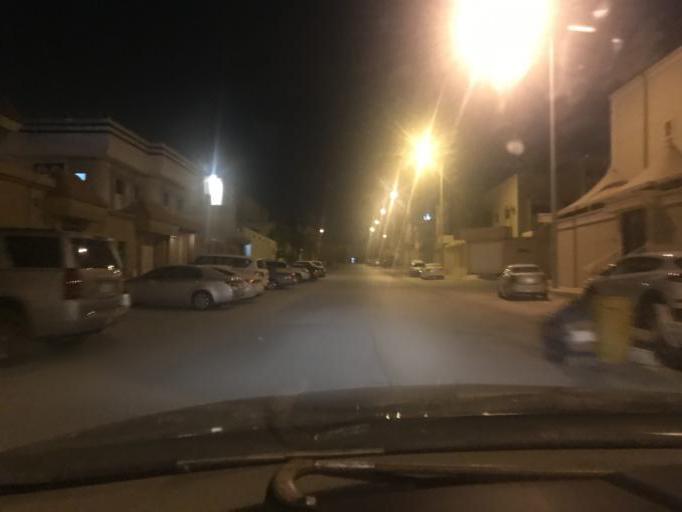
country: SA
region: Ar Riyad
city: Riyadh
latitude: 24.7574
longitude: 46.7624
